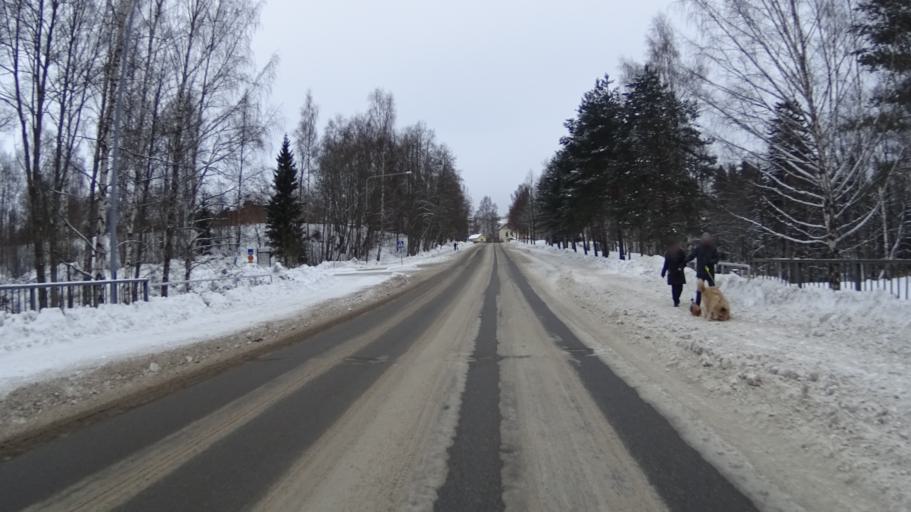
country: FI
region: Uusimaa
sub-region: Helsinki
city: Karkkila
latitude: 60.5306
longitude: 24.2075
